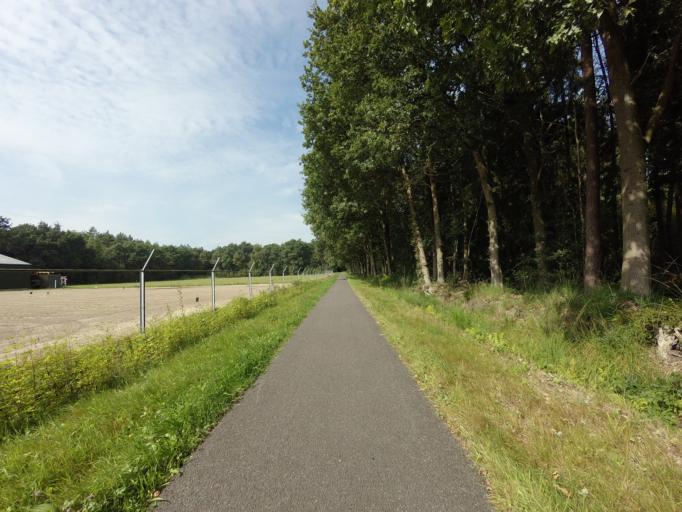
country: NL
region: Drenthe
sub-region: Gemeente Hoogeveen
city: Hoogeveen
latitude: 52.6933
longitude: 6.5750
